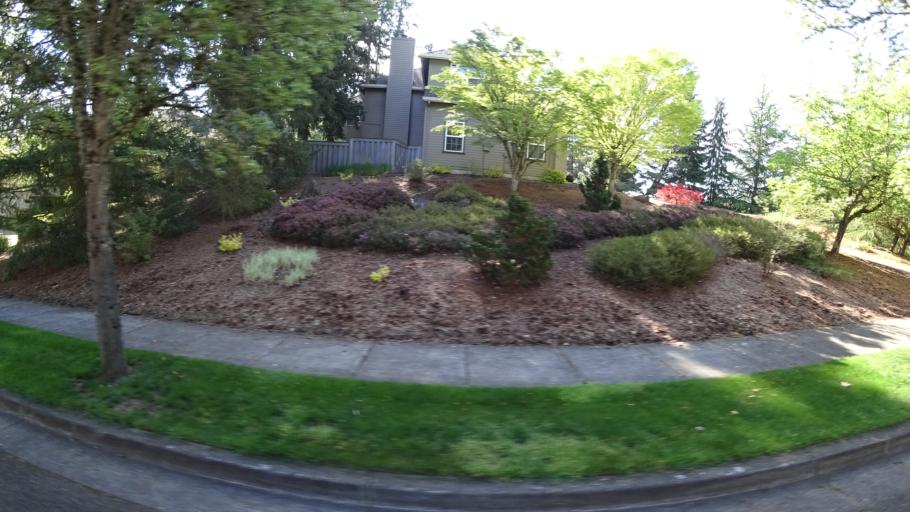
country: US
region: Oregon
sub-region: Washington County
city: King City
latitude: 45.4411
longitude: -122.8367
